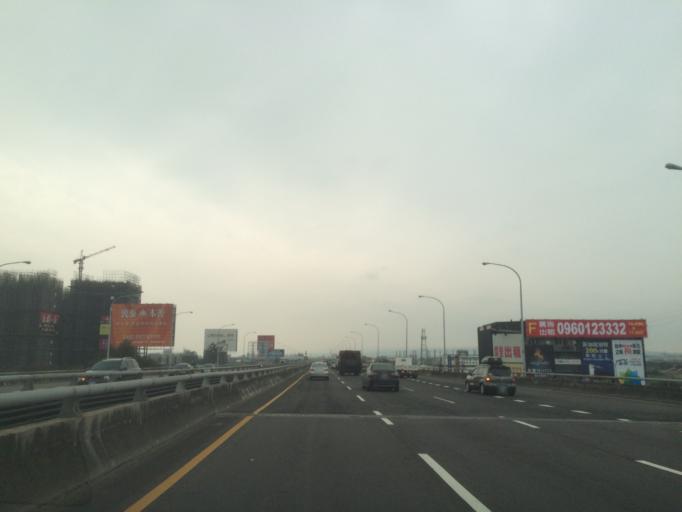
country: TW
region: Taiwan
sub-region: Taichung City
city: Taichung
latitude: 24.1460
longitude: 120.6229
